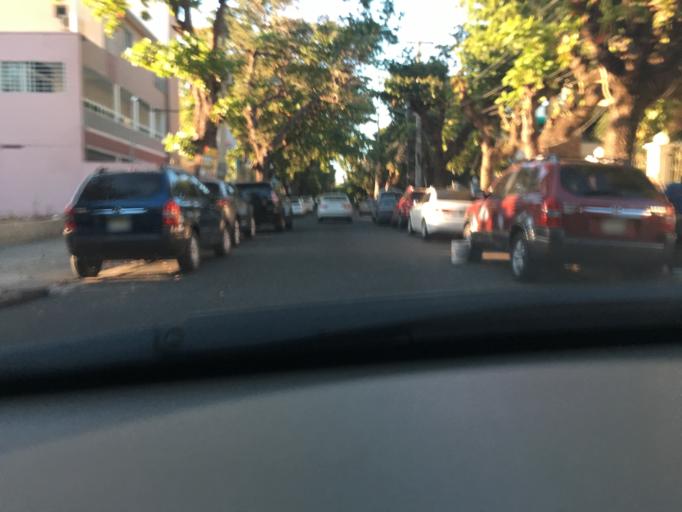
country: DO
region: Nacional
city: Ciudad Nueva
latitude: 18.4663
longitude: -69.8984
